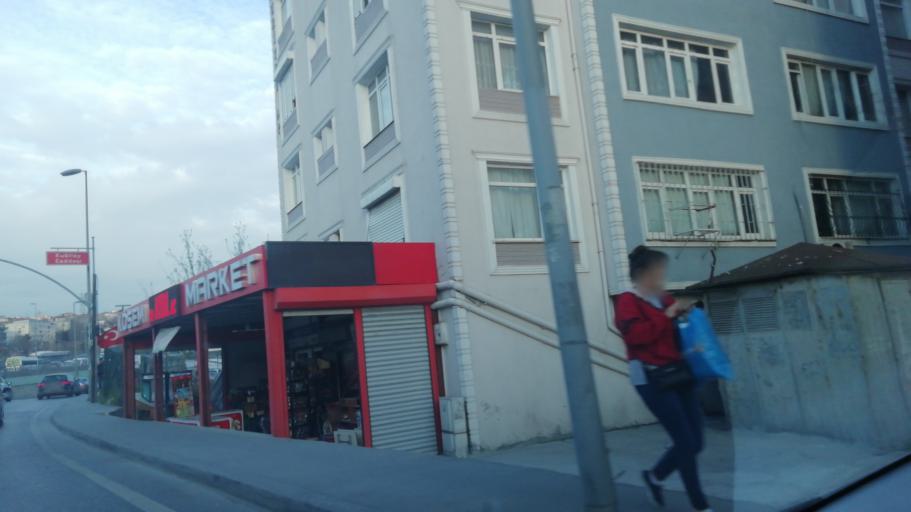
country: TR
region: Istanbul
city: Mahmutbey
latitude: 40.9859
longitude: 28.7698
